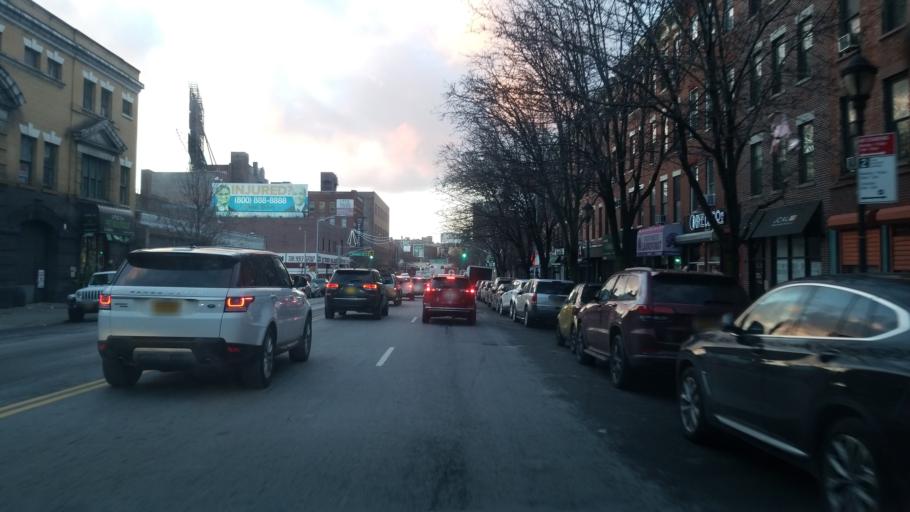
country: US
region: New York
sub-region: New York County
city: Manhattan
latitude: 40.8065
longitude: -73.9265
